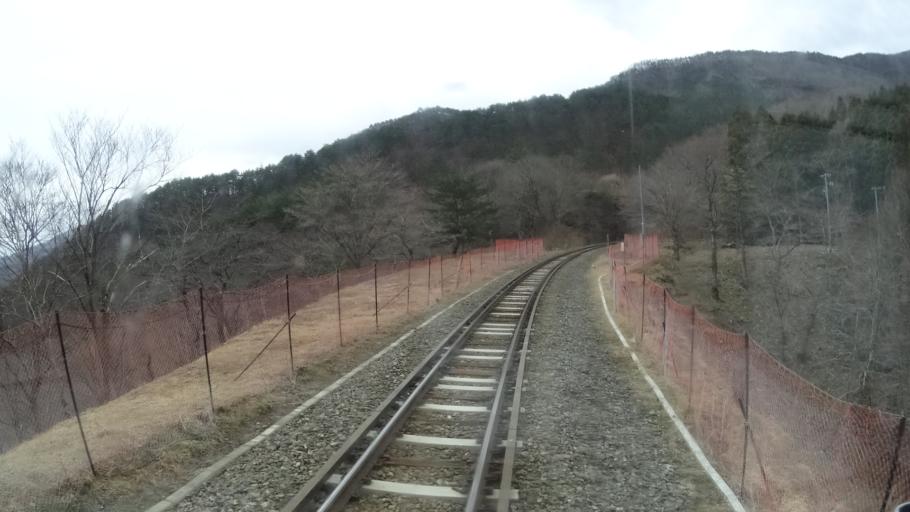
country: JP
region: Iwate
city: Kamaishi
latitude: 39.2552
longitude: 141.7207
